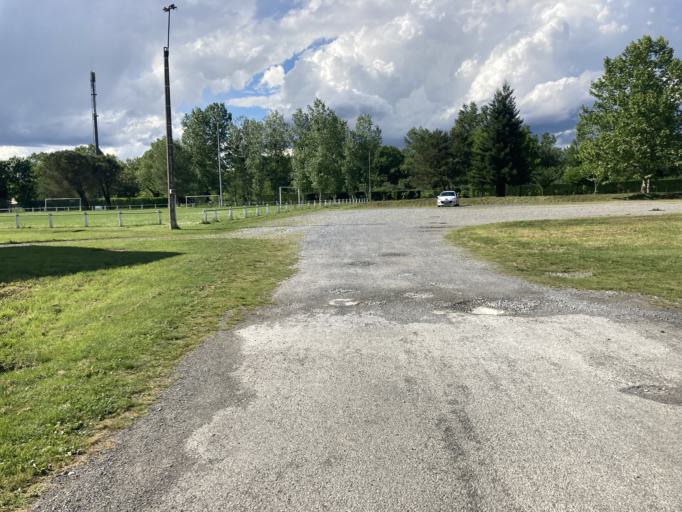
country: FR
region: Aquitaine
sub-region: Departement des Pyrenees-Atlantiques
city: Artiguelouve
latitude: 43.3269
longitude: -0.4755
